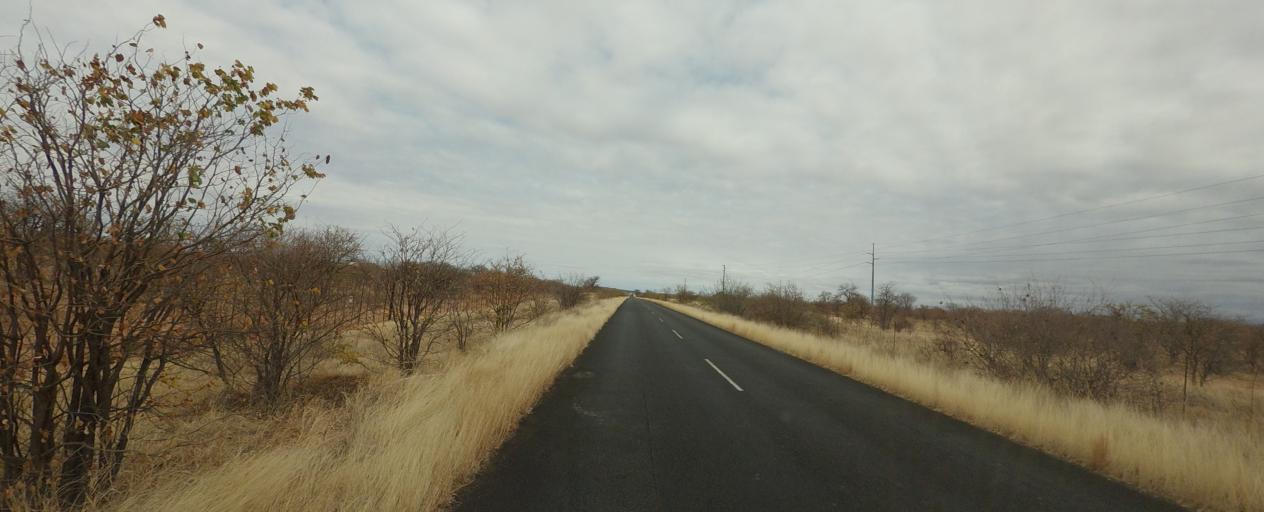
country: ZW
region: Matabeleland South
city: Beitbridge
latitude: -22.4313
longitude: 29.4617
